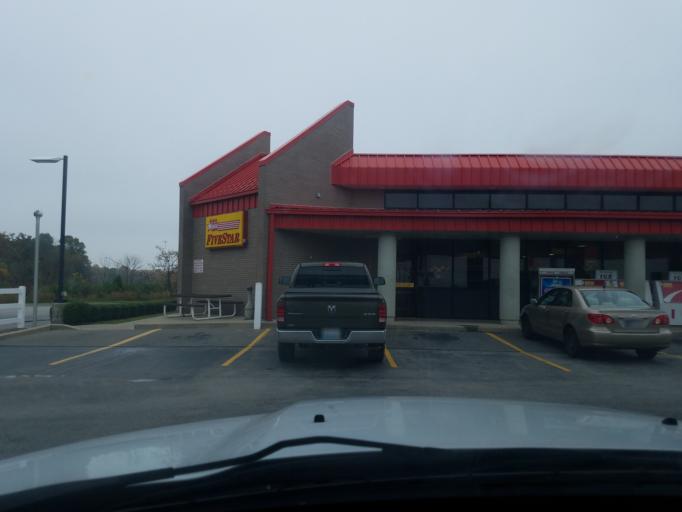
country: US
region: Kentucky
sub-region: Hardin County
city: Elizabethtown
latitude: 37.6716
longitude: -85.8467
